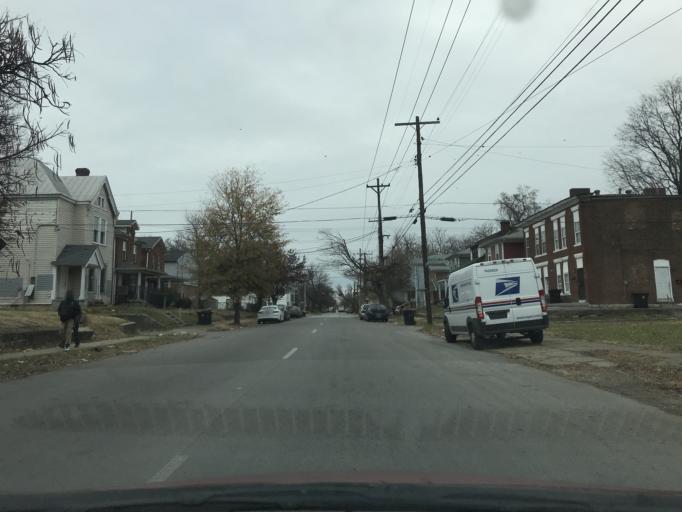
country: US
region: Kentucky
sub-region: Jefferson County
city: Louisville
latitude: 38.2495
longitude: -85.7865
